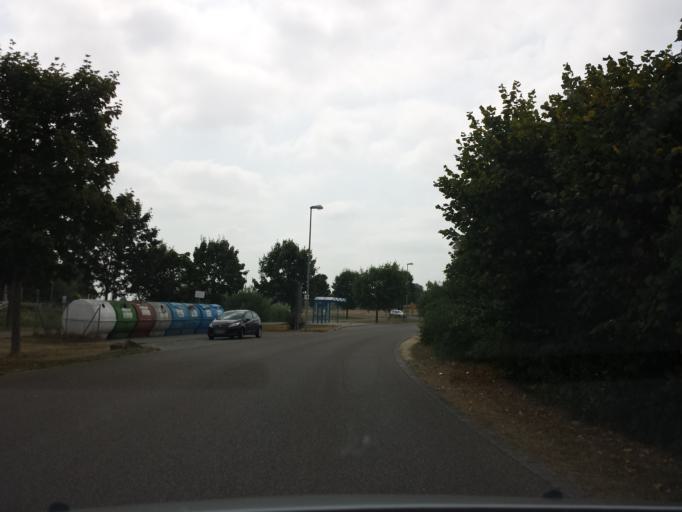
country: DE
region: Bavaria
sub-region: Swabia
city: Wasserburg
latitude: 48.4487
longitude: 10.2630
